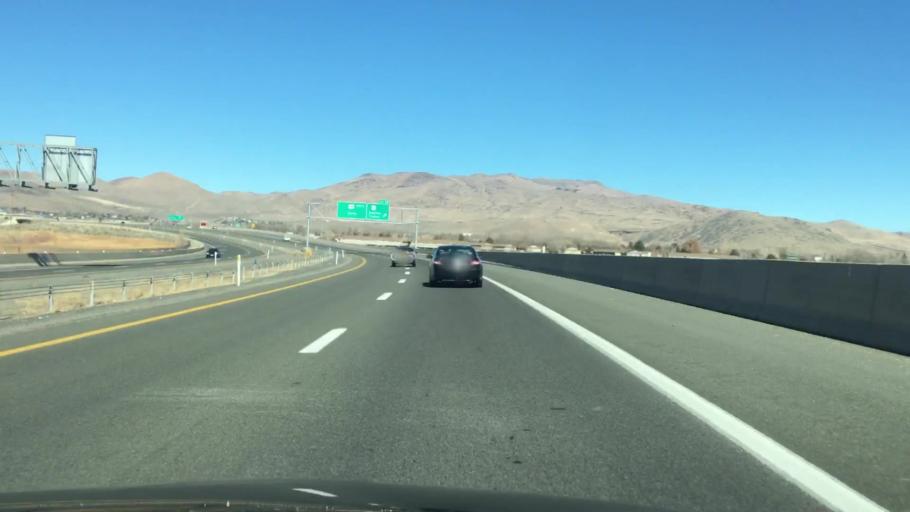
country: US
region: Nevada
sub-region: Carson City
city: Carson City
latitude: 39.1671
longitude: -119.7380
